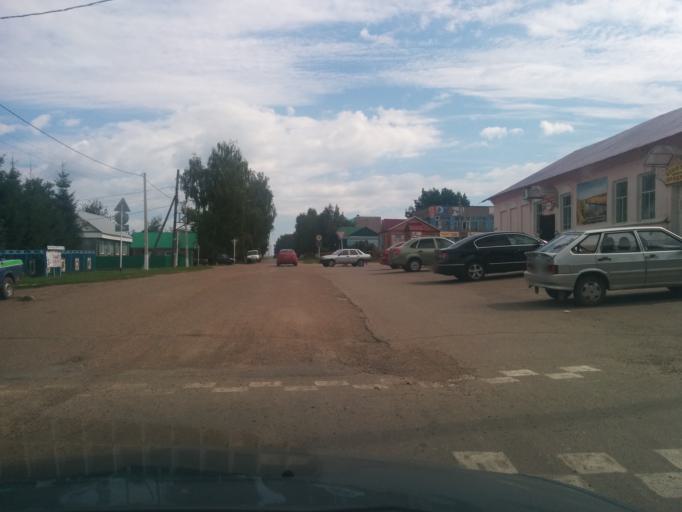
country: RU
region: Bashkortostan
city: Ulukulevo
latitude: 54.4097
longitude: 56.7849
